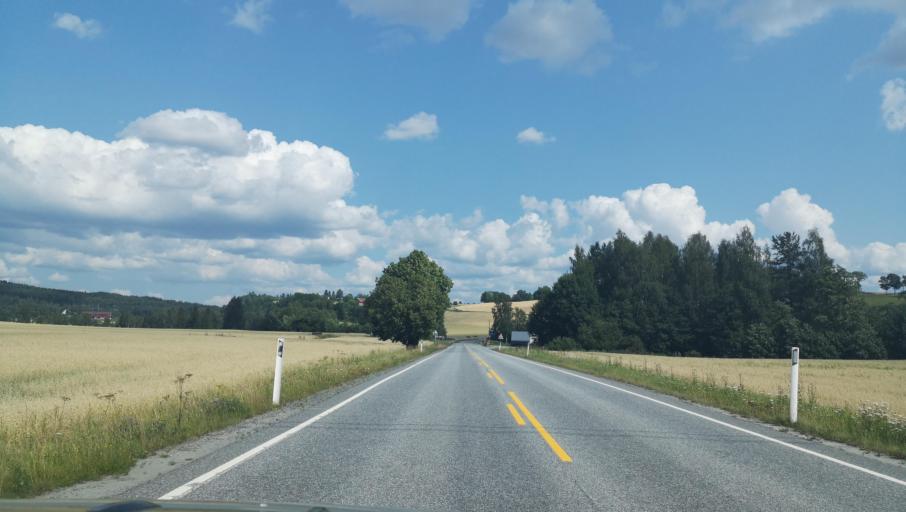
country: NO
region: Buskerud
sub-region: Ovre Eiker
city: Hokksund
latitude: 59.7238
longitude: 9.8316
